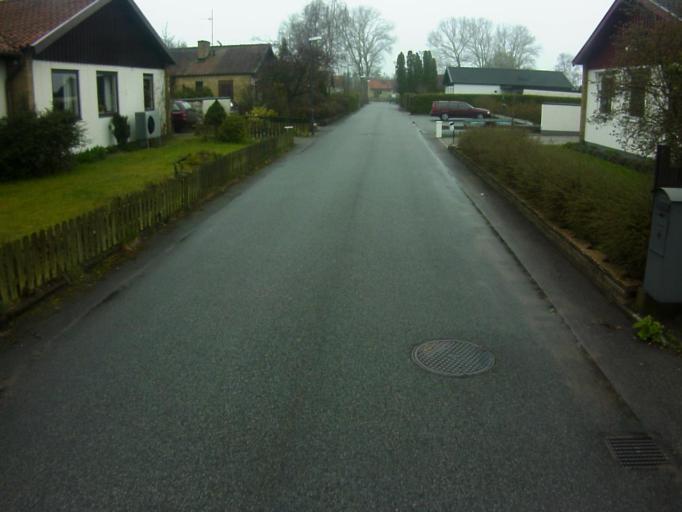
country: SE
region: Skane
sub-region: Kavlinge Kommun
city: Kaevlinge
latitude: 55.7788
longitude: 13.0897
